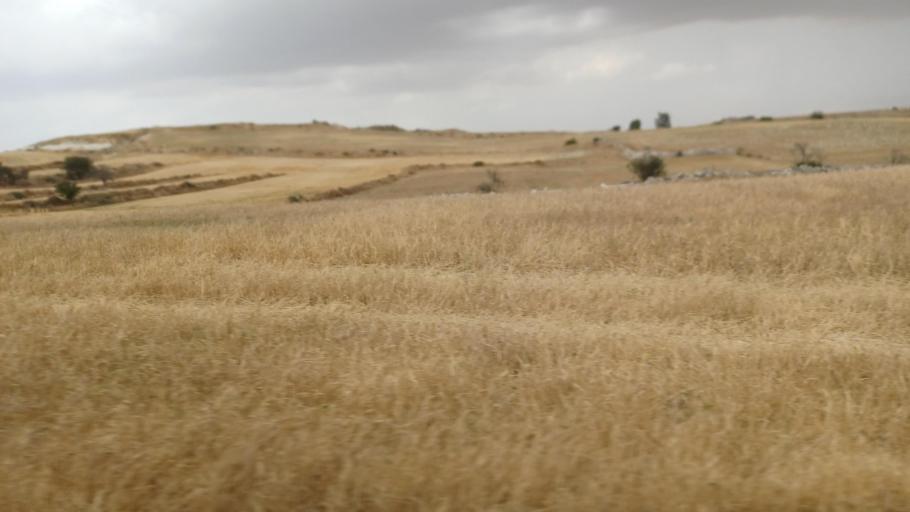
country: CY
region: Larnaka
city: Athienou
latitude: 35.0329
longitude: 33.5700
